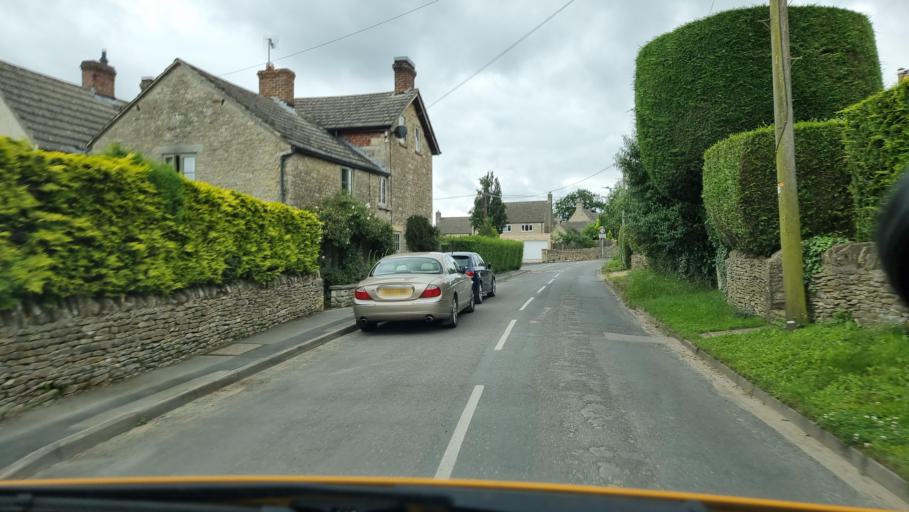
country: GB
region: England
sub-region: Oxfordshire
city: North Leigh
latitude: 51.8152
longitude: -1.4428
